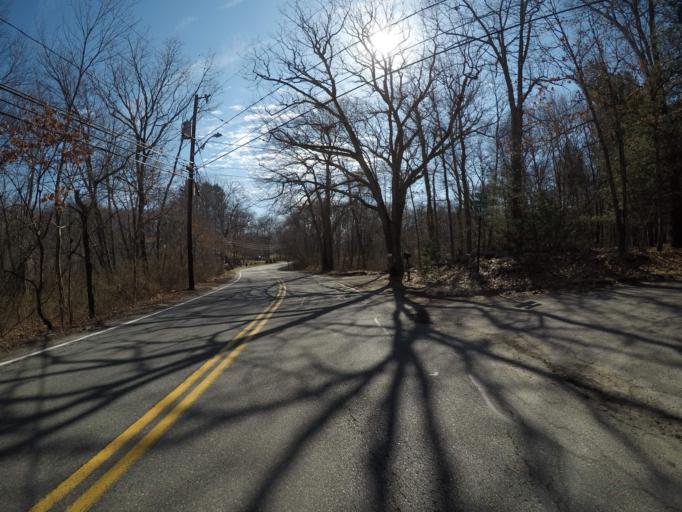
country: US
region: Massachusetts
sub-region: Norfolk County
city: Stoughton
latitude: 42.0846
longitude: -71.1394
